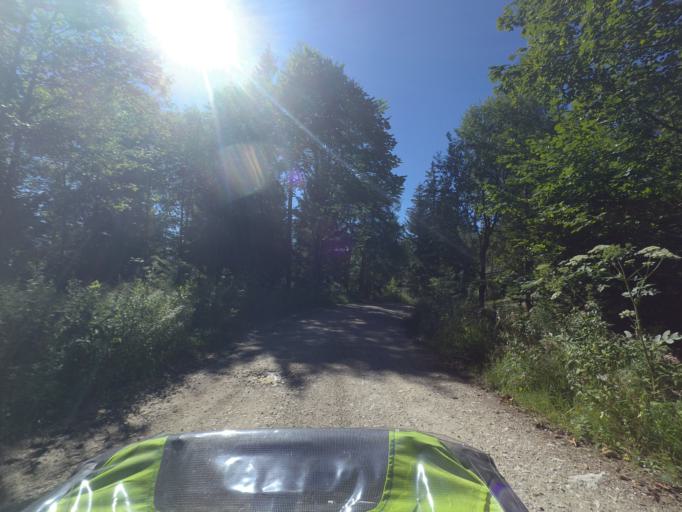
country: AT
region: Salzburg
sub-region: Politischer Bezirk Hallein
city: Hallein
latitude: 47.6528
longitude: 13.1012
